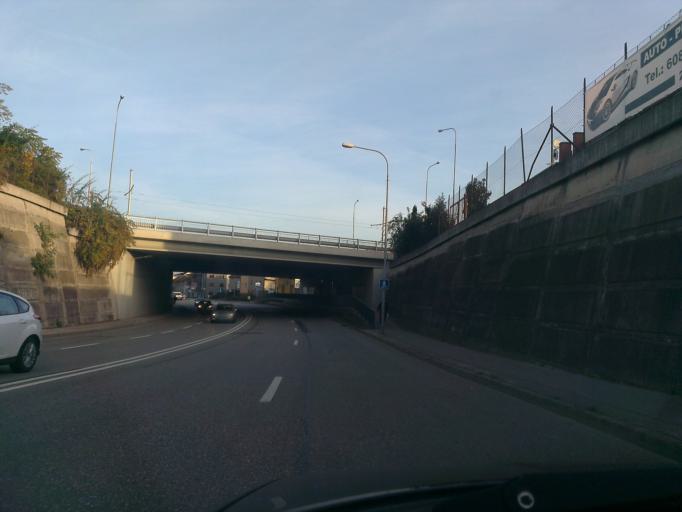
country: CZ
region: South Moravian
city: Moravany
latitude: 49.1630
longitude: 16.5981
